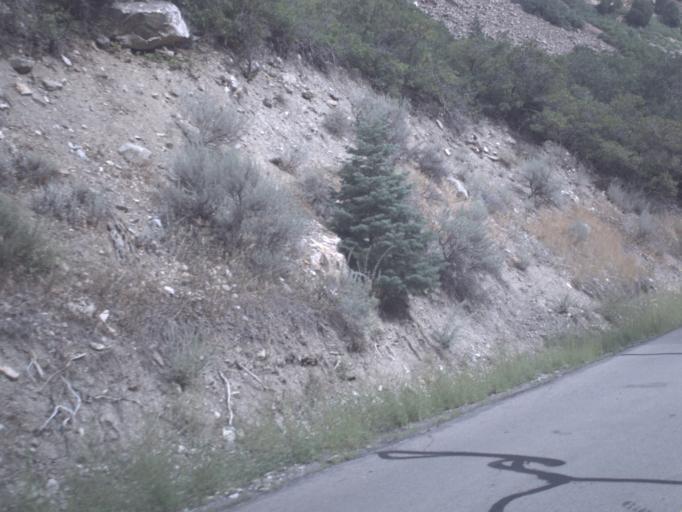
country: US
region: Utah
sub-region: Utah County
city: Cedar Hills
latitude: 40.4390
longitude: -111.7205
